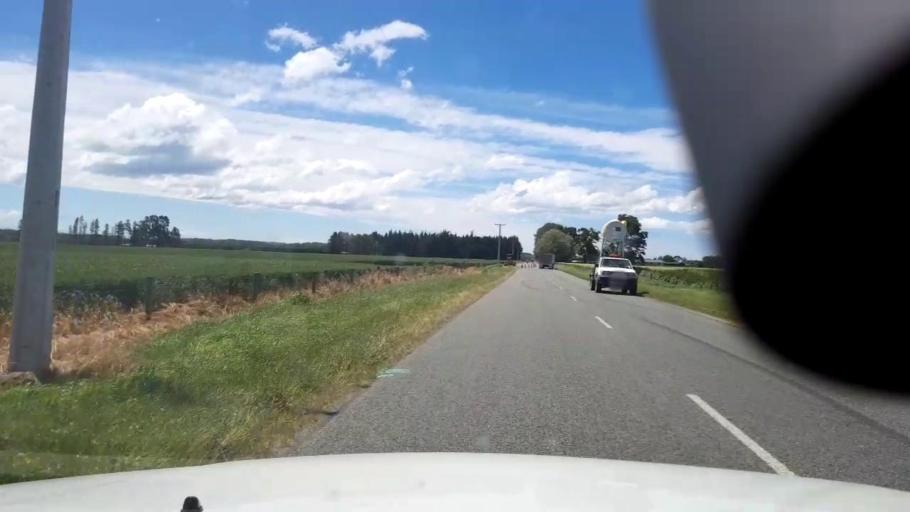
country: NZ
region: Canterbury
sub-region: Timaru District
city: Pleasant Point
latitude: -44.2803
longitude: 171.2460
